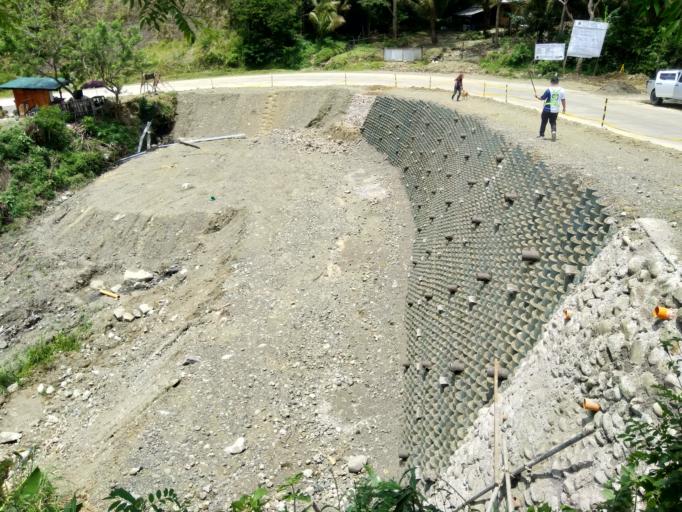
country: PH
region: Davao
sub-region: Province of Davao del Norte
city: Santo Nino
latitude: 7.6308
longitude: 125.4977
